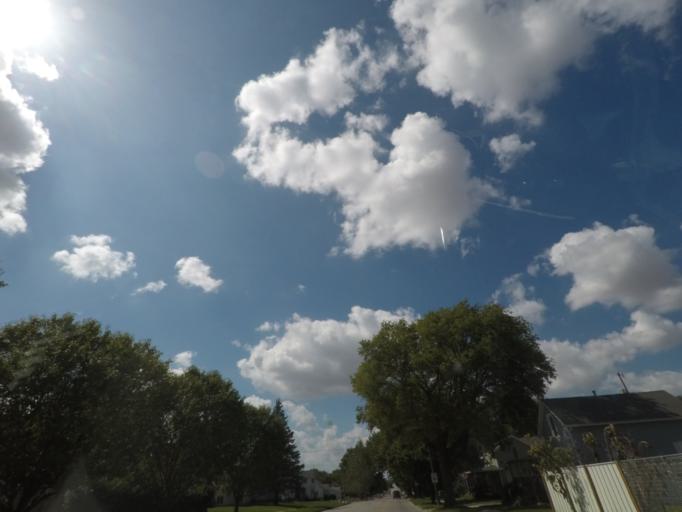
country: US
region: Iowa
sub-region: Story County
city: Nevada
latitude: 42.0228
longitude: -93.4552
